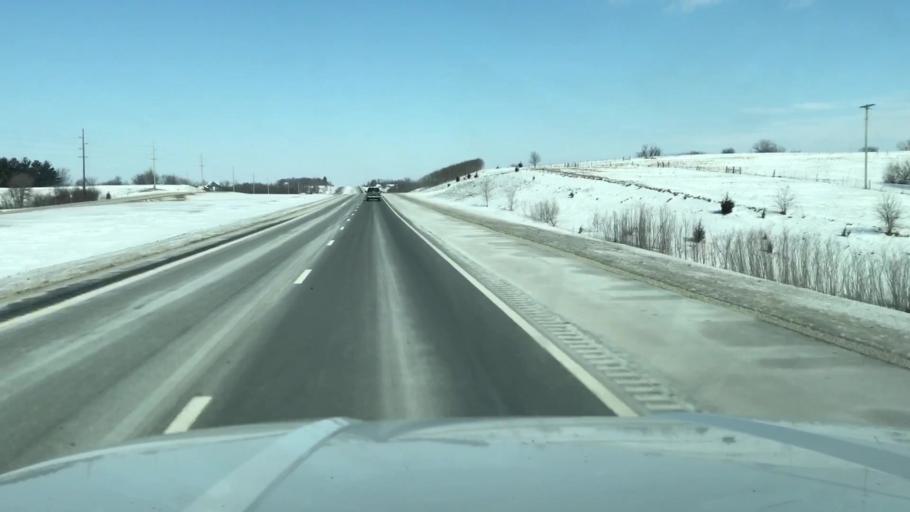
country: US
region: Missouri
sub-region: Nodaway County
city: Maryville
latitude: 40.1894
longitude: -94.8678
